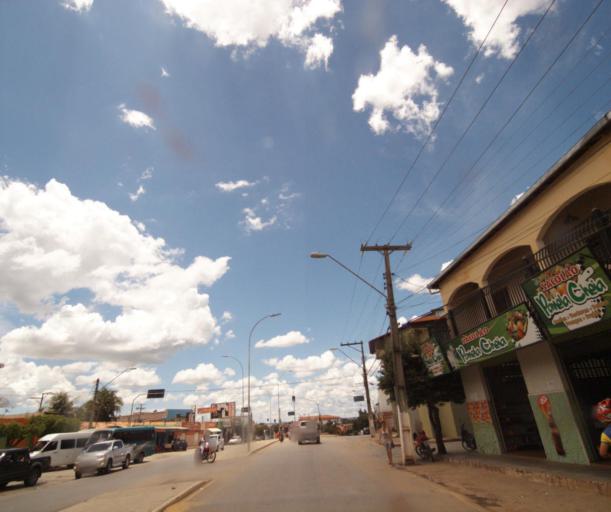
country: BR
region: Bahia
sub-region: Sao Felix Do Coribe
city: Santa Maria da Vitoria
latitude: -13.4047
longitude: -44.1929
